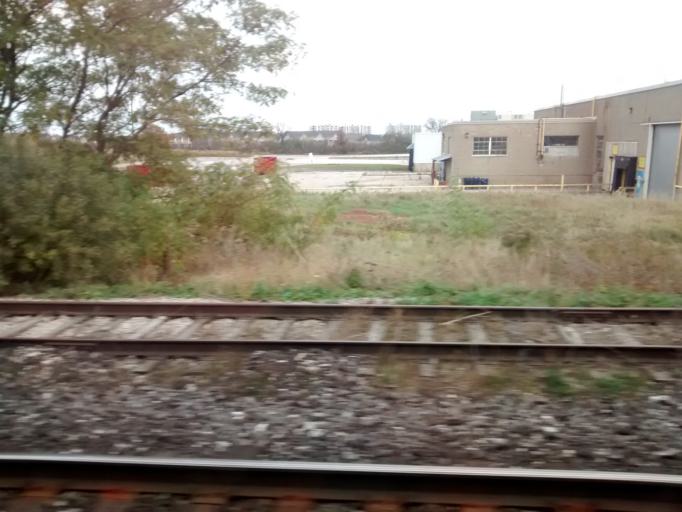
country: CA
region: Ontario
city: Burlington
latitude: 43.3771
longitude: -79.7633
